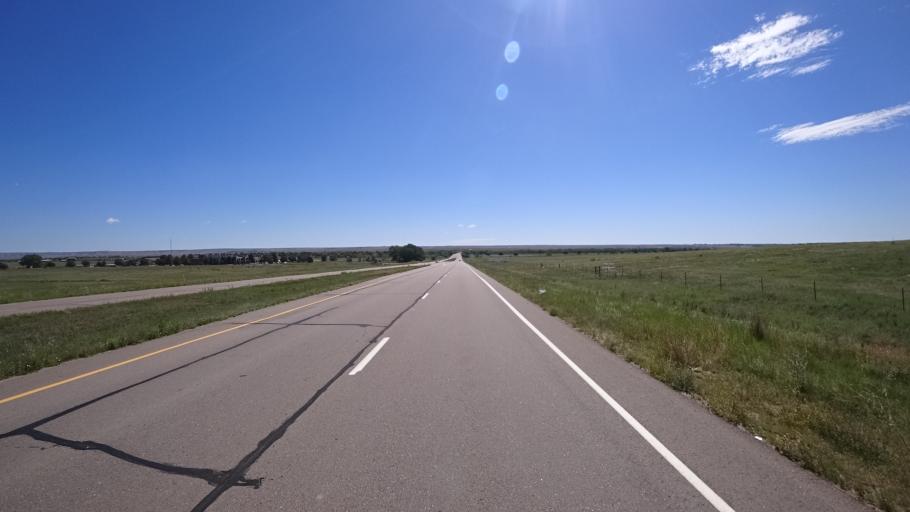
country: US
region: Colorado
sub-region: El Paso County
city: Security-Widefield
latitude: 38.7622
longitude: -104.6727
